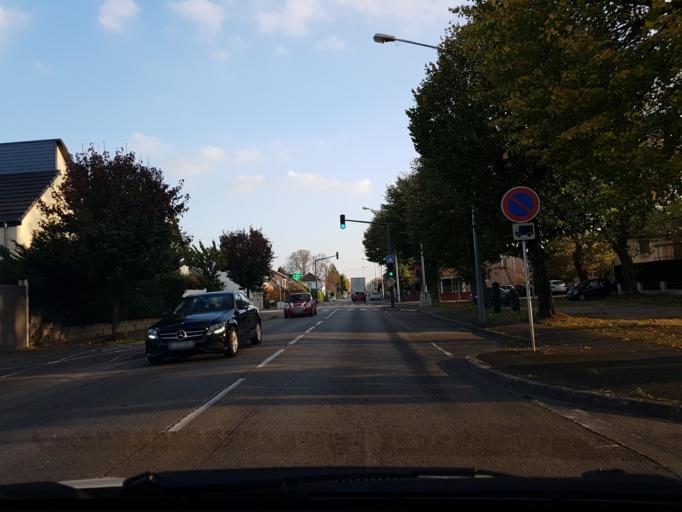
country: FR
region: Alsace
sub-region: Departement du Haut-Rhin
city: Rixheim
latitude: 47.7661
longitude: 7.3935
